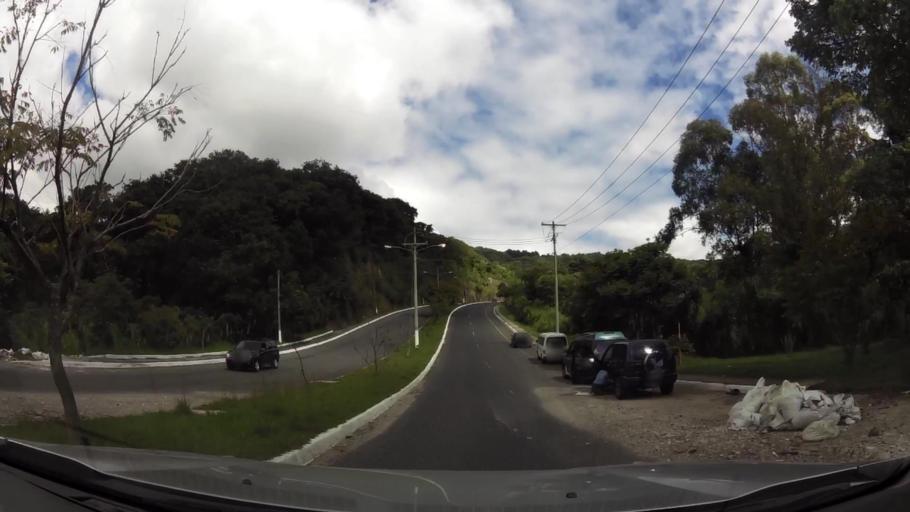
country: GT
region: Guatemala
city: Guatemala City
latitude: 14.6484
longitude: -90.5583
